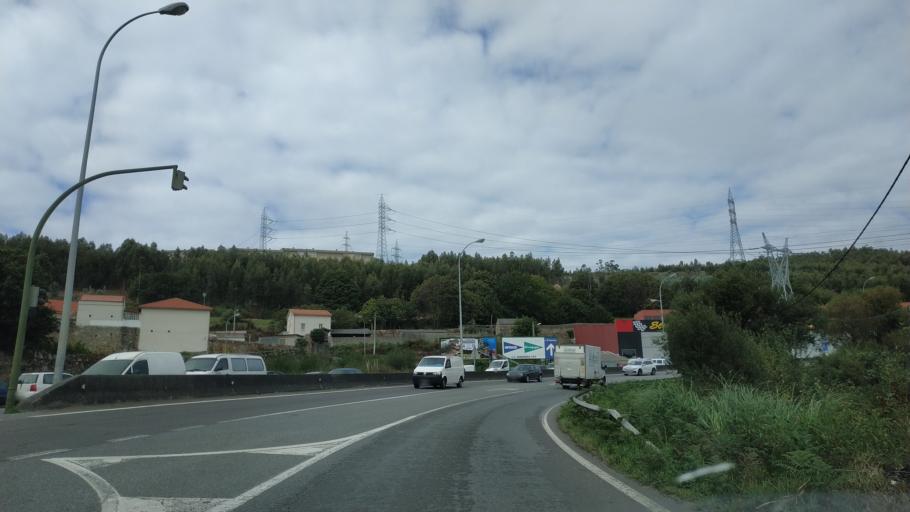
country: ES
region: Galicia
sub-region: Provincia da Coruna
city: Arteixo
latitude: 43.3238
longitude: -8.4755
